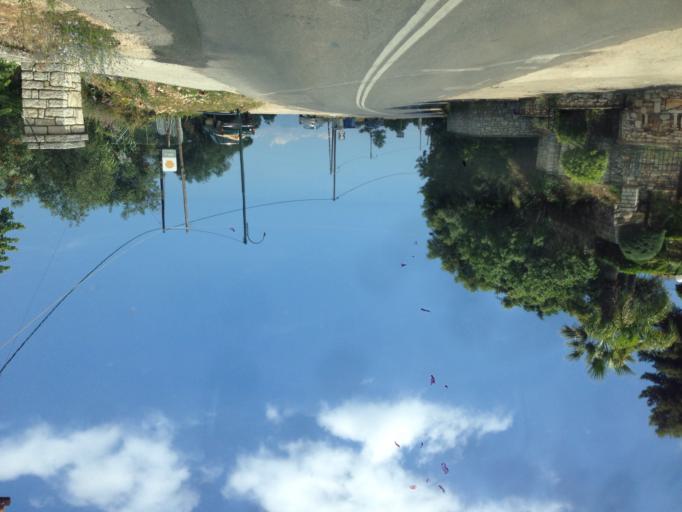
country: GR
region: Ionian Islands
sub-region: Nomos Kerkyras
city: Acharavi
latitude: 39.7762
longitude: 19.9283
